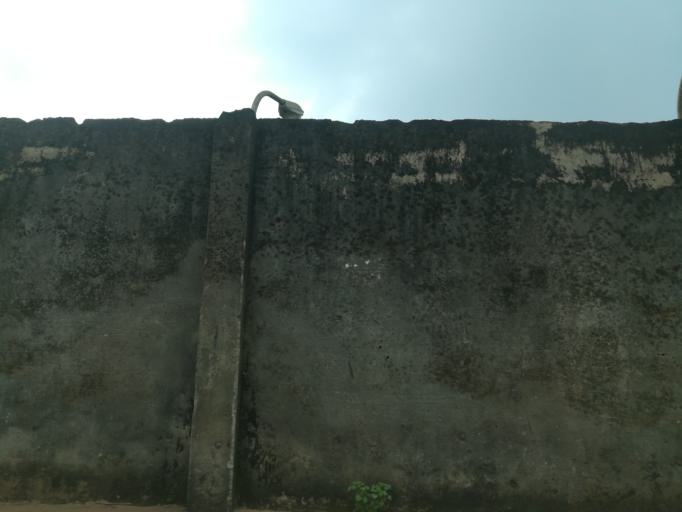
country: NG
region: Lagos
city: Ikorodu
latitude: 6.6164
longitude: 3.5218
